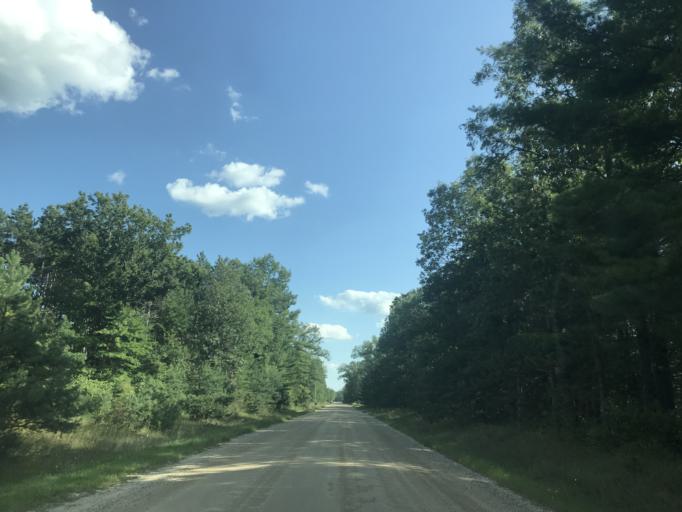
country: US
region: Michigan
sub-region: Newaygo County
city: Newaygo
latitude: 43.4463
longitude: -85.7326
